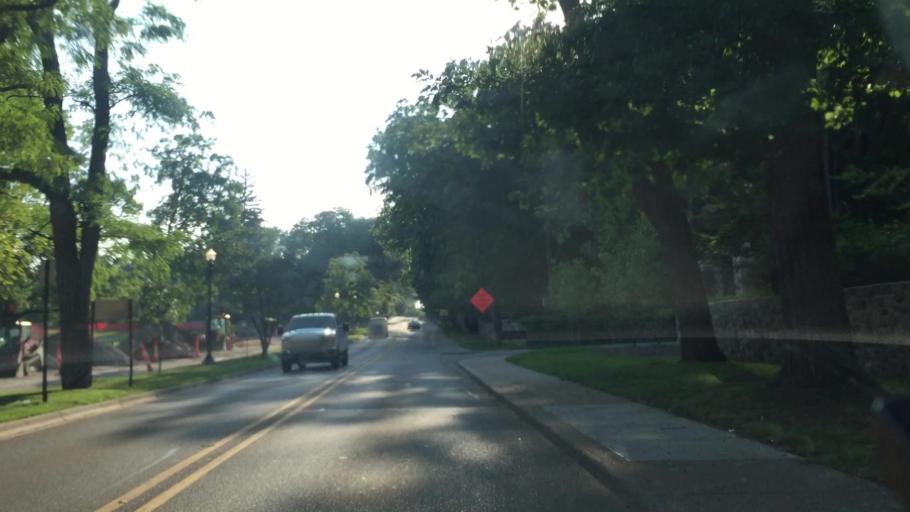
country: US
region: Michigan
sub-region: Oakland County
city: Bloomfield Hills
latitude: 42.5674
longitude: -83.2453
